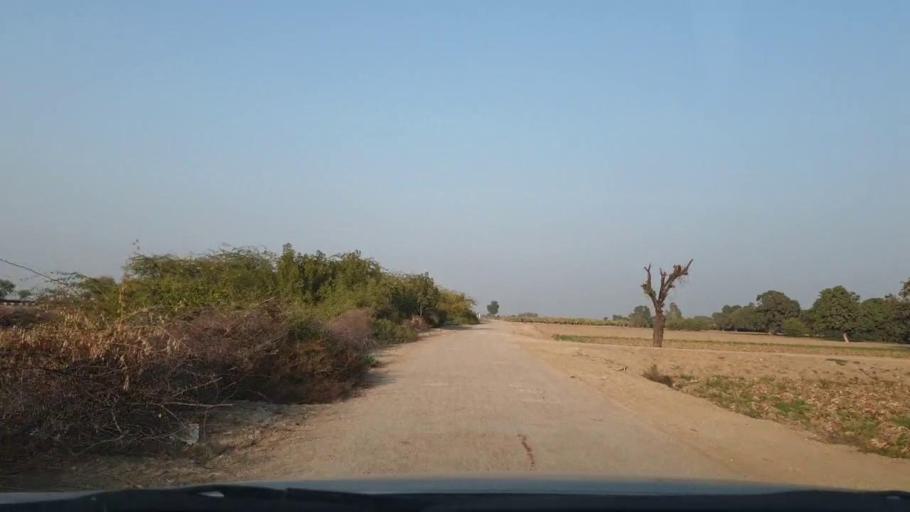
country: PK
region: Sindh
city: Tando Adam
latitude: 25.6975
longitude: 68.6371
